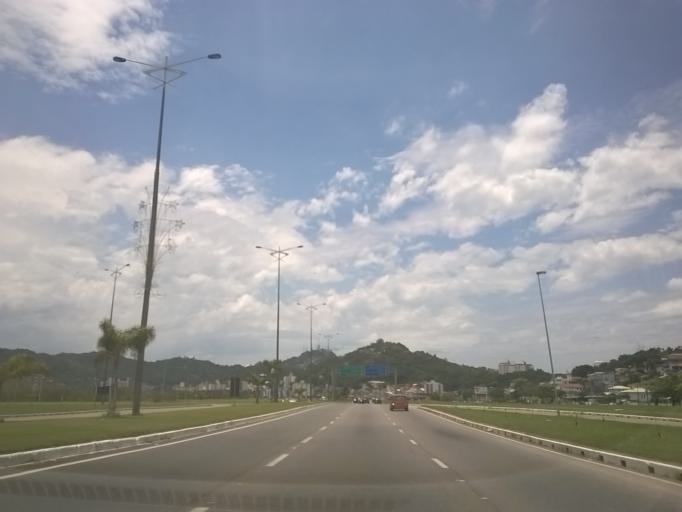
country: BR
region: Santa Catarina
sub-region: Florianopolis
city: Saco dos Limoes
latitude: -27.6202
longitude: -48.5280
